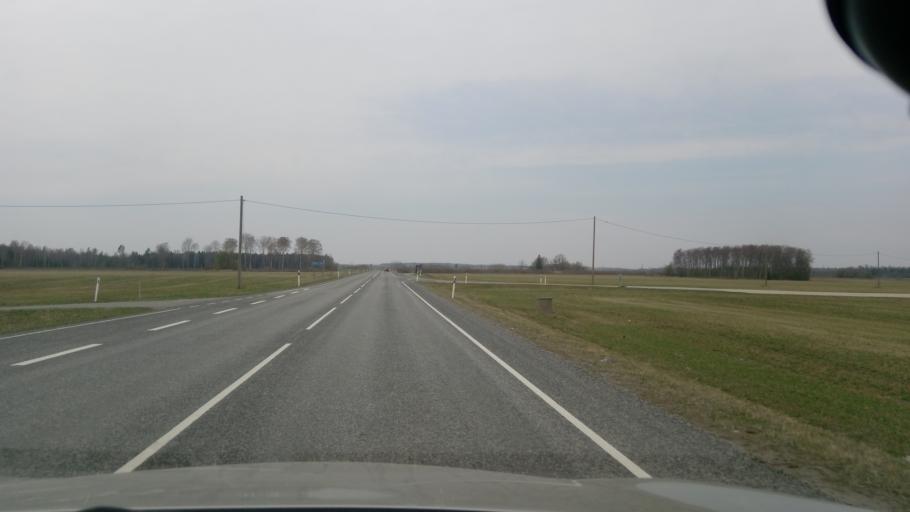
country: EE
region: Jaervamaa
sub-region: Tueri vald
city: Sarevere
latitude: 58.7708
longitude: 25.5214
